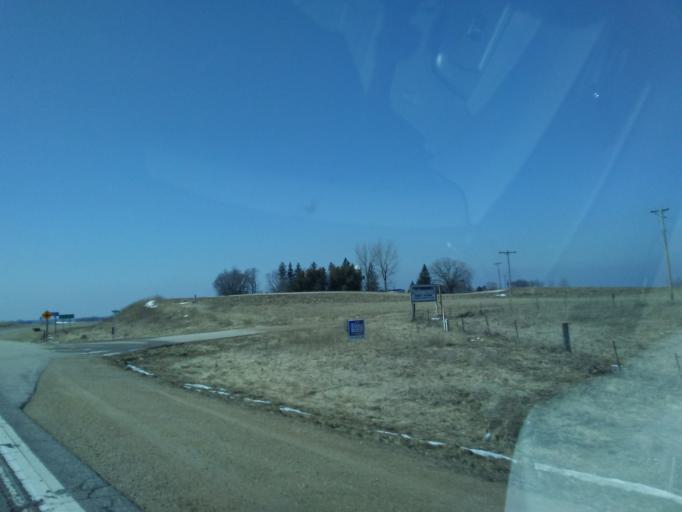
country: US
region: Wisconsin
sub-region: Vernon County
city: Westby
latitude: 43.6573
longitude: -90.9124
